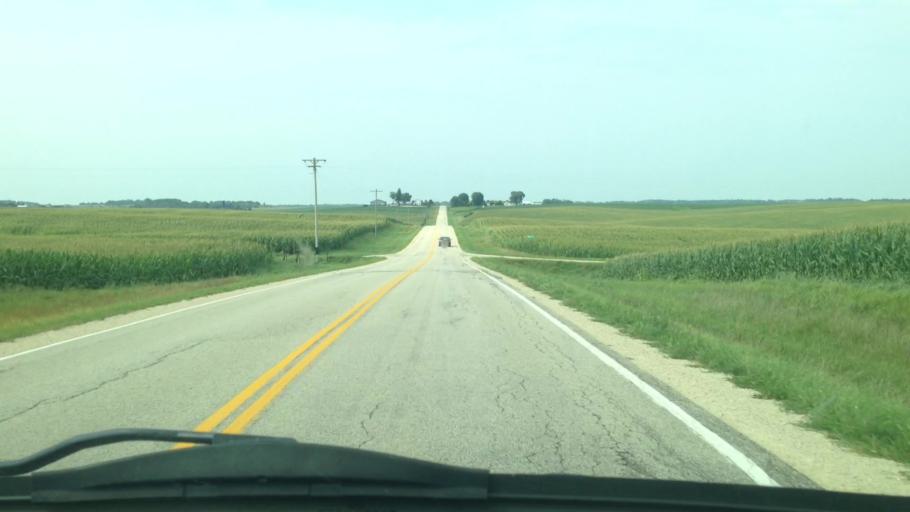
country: US
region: Minnesota
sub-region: Winona County
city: Lewiston
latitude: 43.8821
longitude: -91.9594
